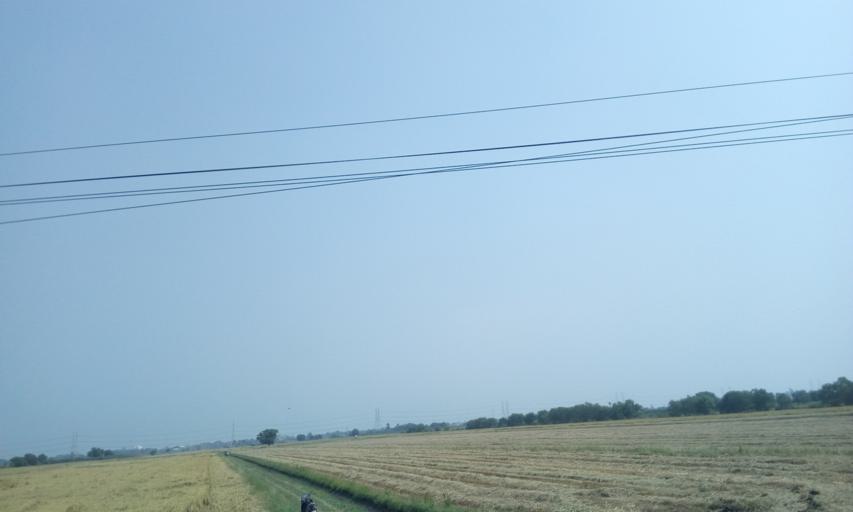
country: TH
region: Pathum Thani
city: Ban Lam Luk Ka
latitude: 13.9824
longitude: 100.7548
